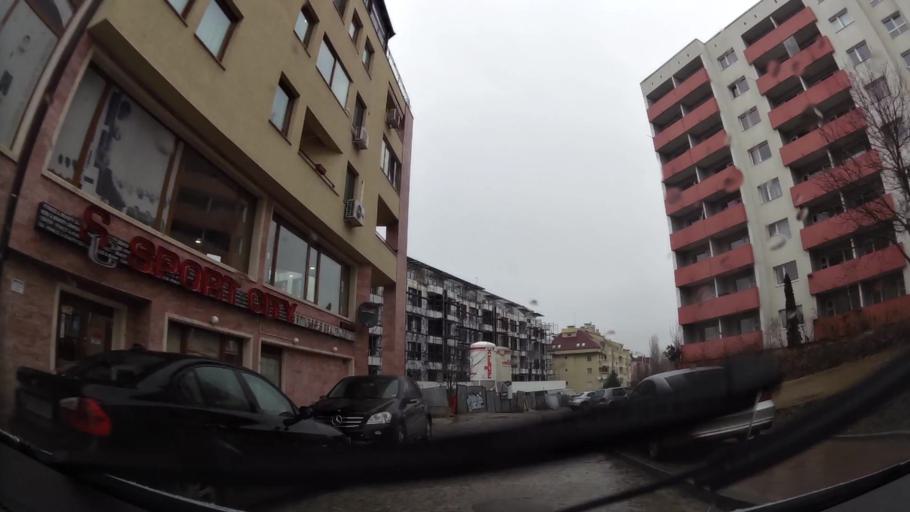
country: BG
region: Sofia-Capital
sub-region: Stolichna Obshtina
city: Sofia
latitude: 42.6538
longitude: 23.3398
